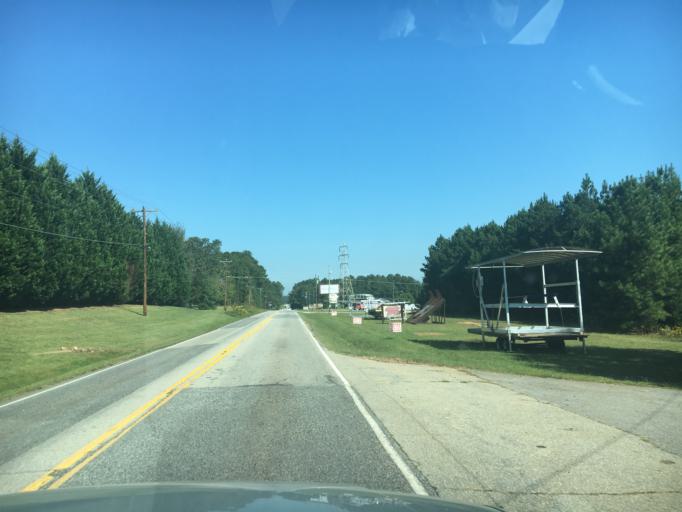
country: US
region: South Carolina
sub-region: Spartanburg County
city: Inman
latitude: 35.0999
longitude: -82.0401
